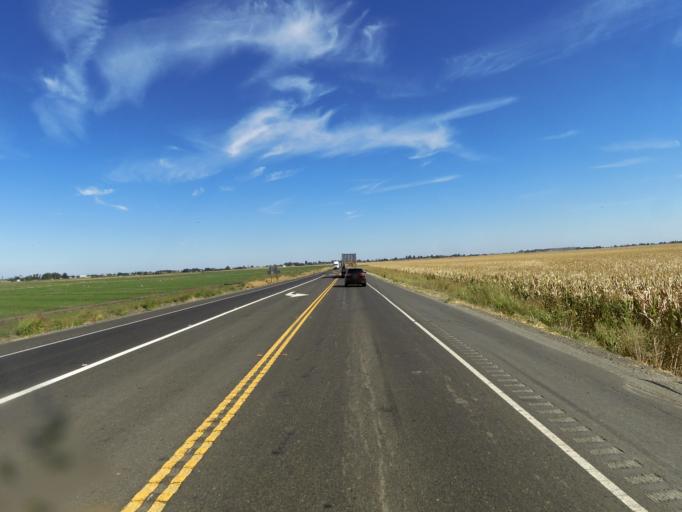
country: US
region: California
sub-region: Solano County
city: Rio Vista
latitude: 38.1398
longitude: -121.6232
